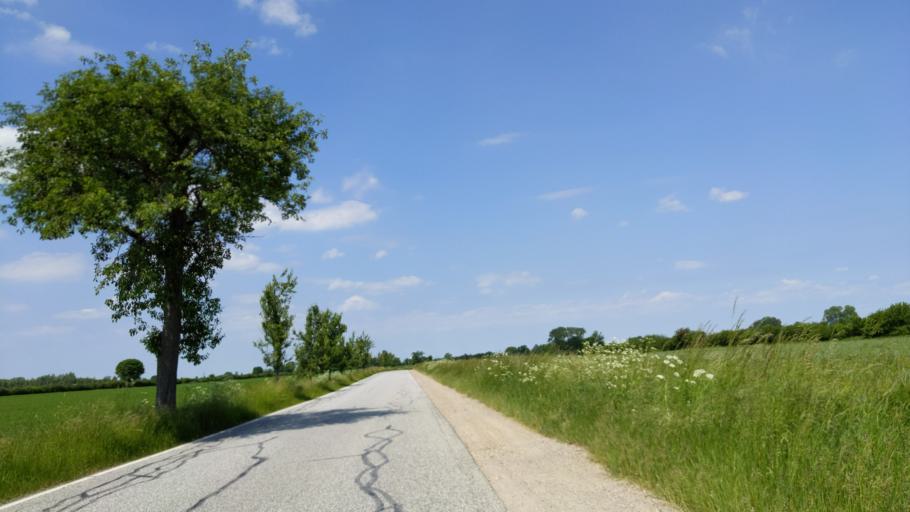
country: DE
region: Schleswig-Holstein
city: Krummesse
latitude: 53.8187
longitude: 10.6711
